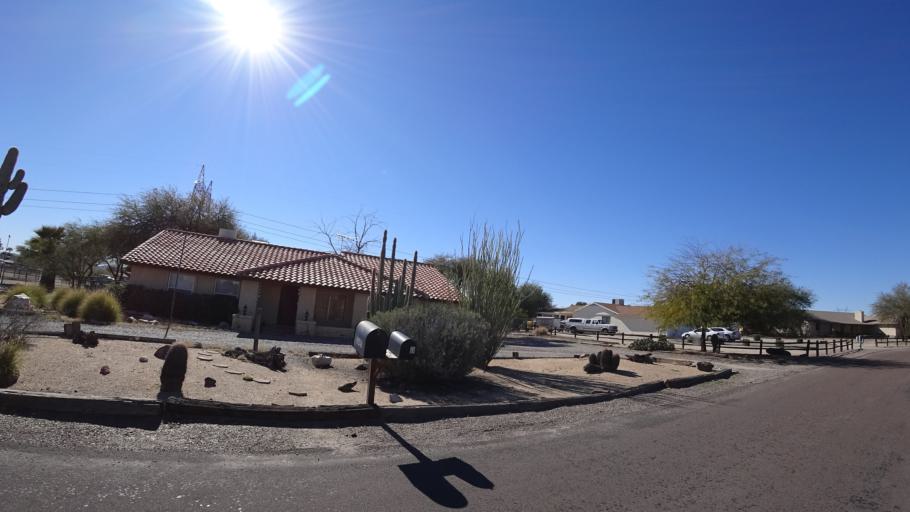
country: US
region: Arizona
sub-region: Maricopa County
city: Buckeye
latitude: 33.4258
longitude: -112.5337
